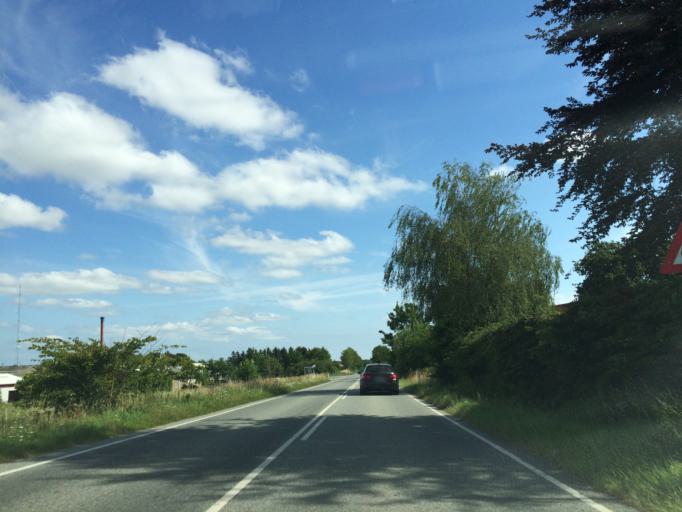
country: DK
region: Central Jutland
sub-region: Syddjurs Kommune
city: Ronde
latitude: 56.3097
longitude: 10.4430
